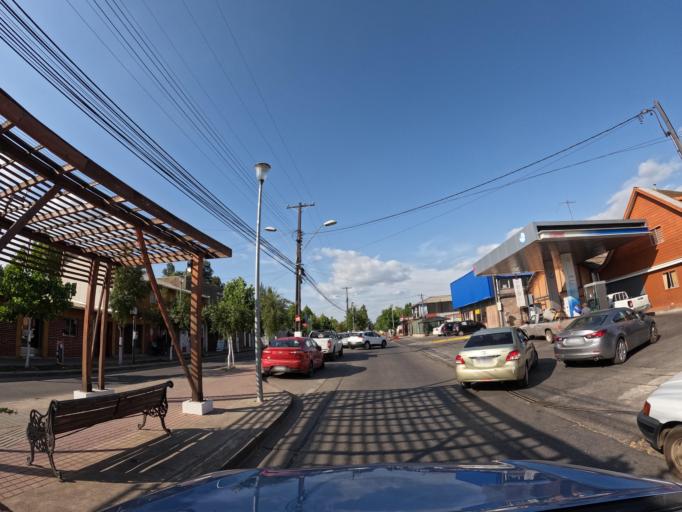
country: CL
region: Maule
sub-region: Provincia de Curico
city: Molina
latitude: -35.2837
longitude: -71.2603
